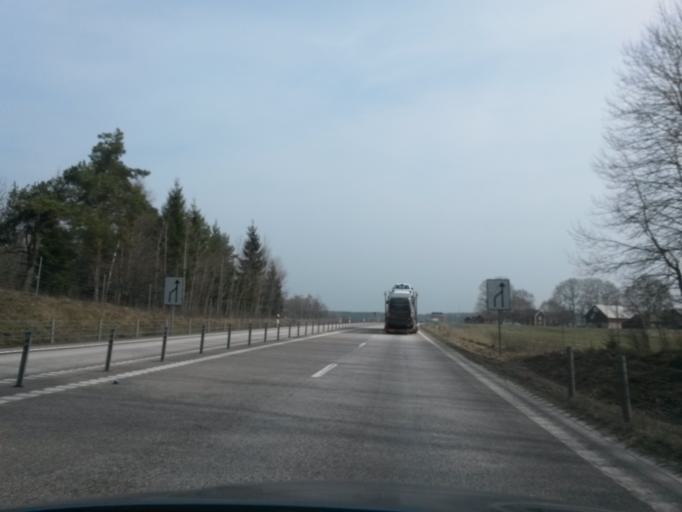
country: SE
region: Vaestra Goetaland
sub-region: Gullspangs Kommun
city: Hova
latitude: 58.8203
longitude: 14.1448
